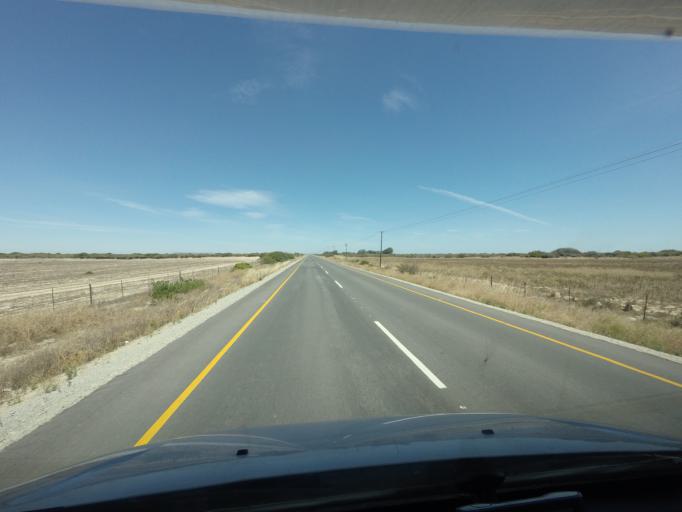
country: ZA
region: Western Cape
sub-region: West Coast District Municipality
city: Vredenburg
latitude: -32.7960
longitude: 18.2556
